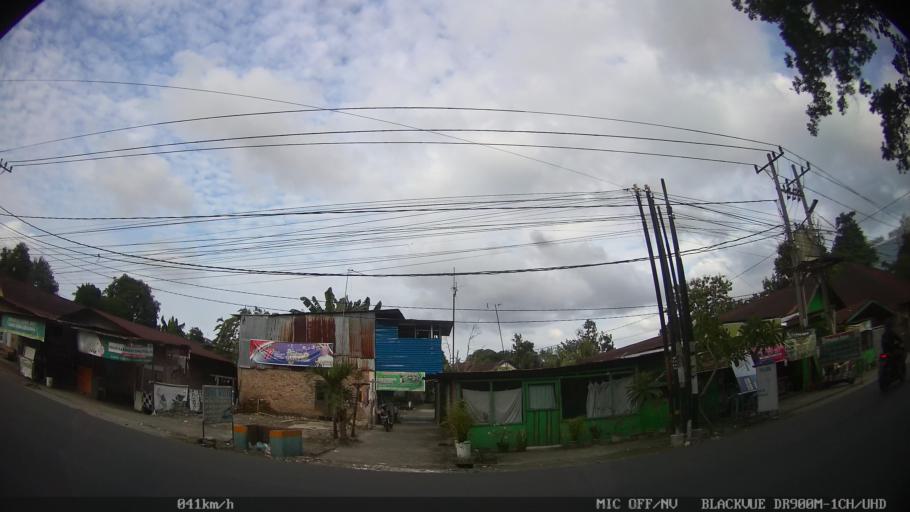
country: ID
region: North Sumatra
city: Medan
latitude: 3.6006
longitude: 98.6771
